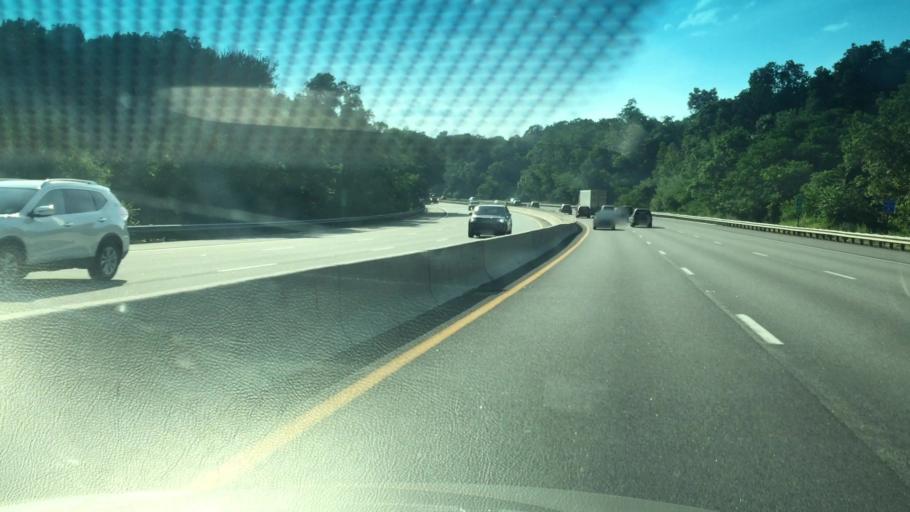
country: US
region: New Jersey
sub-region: Morris County
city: Budd Lake
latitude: 40.9149
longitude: -74.7629
